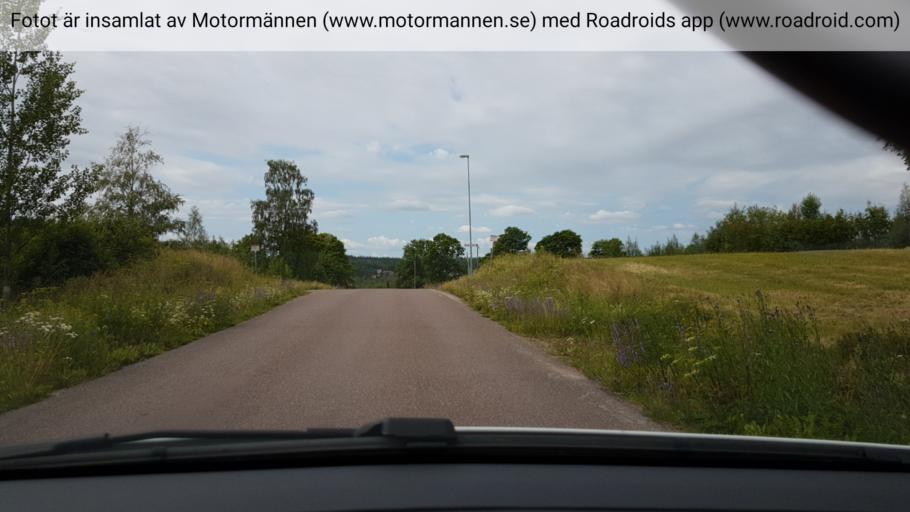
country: SE
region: Dalarna
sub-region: Rattviks Kommun
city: Raettvik
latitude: 60.9240
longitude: 15.1106
